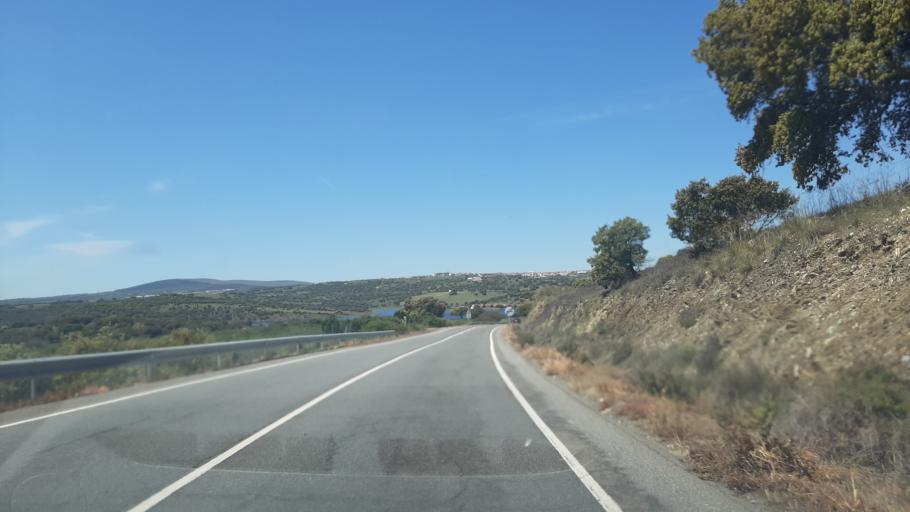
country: ES
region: Castille and Leon
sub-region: Provincia de Salamanca
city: Guijo de Avila
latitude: 40.5486
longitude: -5.6165
